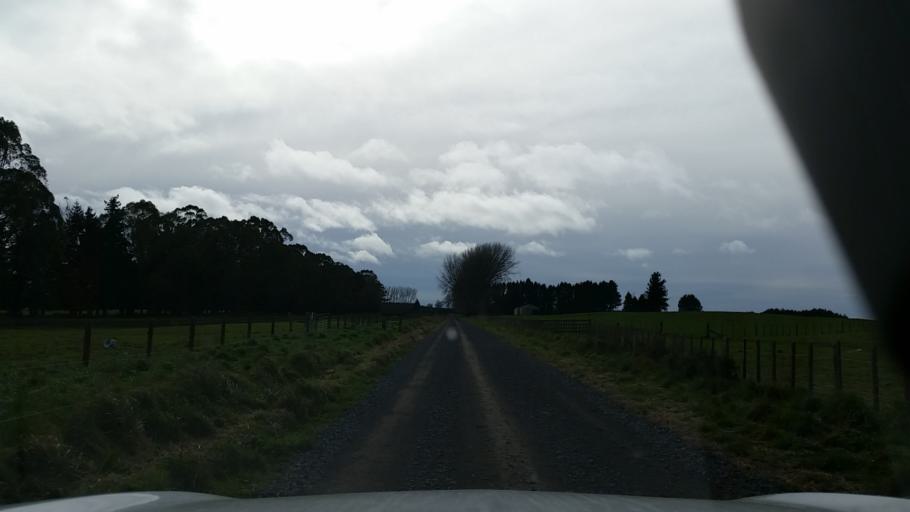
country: NZ
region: Bay of Plenty
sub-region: Whakatane District
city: Murupara
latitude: -38.4757
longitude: 176.4155
